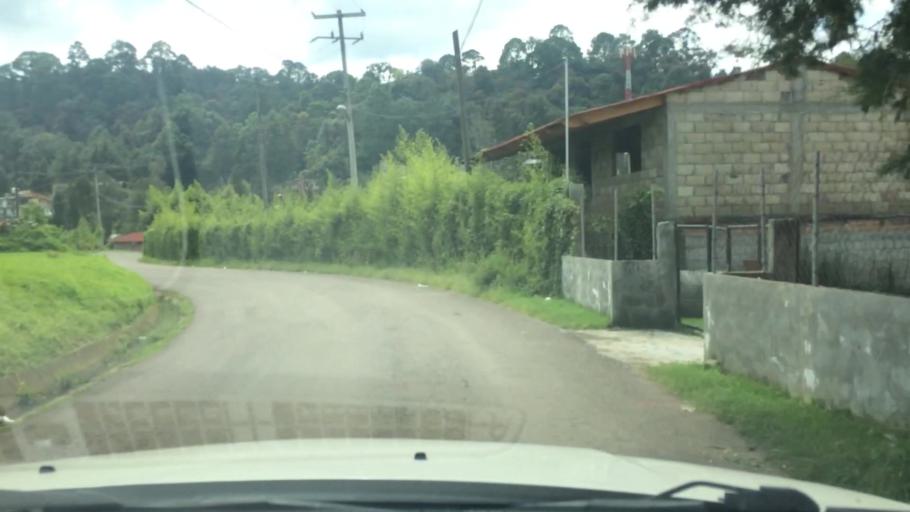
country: MX
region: Mexico
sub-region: Valle de Bravo
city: Cuadrilla de Dolores
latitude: 19.1520
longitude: -100.0582
